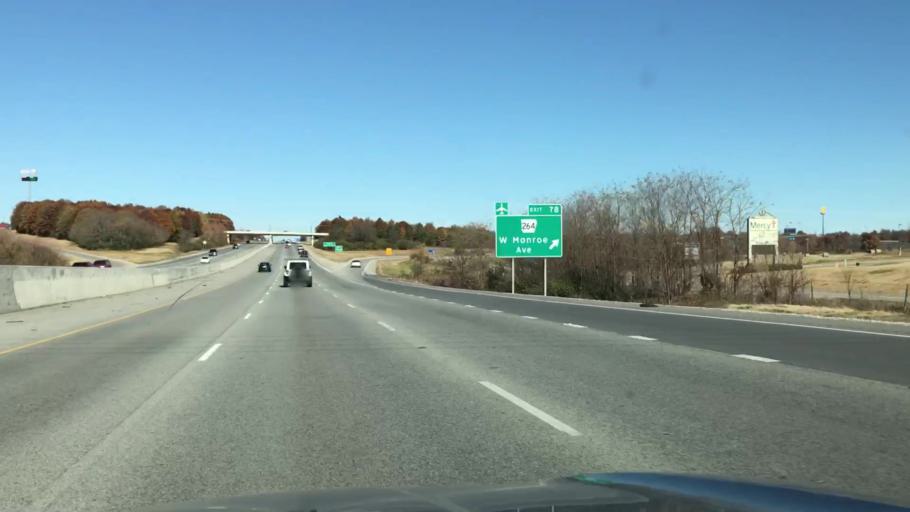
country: US
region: Arkansas
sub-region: Benton County
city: Lowell
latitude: 36.2493
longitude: -94.1504
